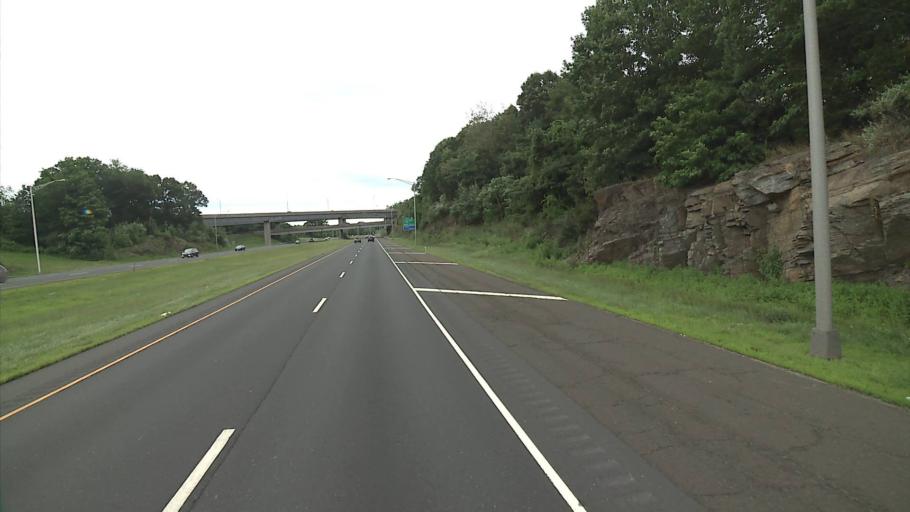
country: US
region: Connecticut
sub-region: Fairfield County
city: Trumbull
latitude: 41.2395
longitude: -73.1529
